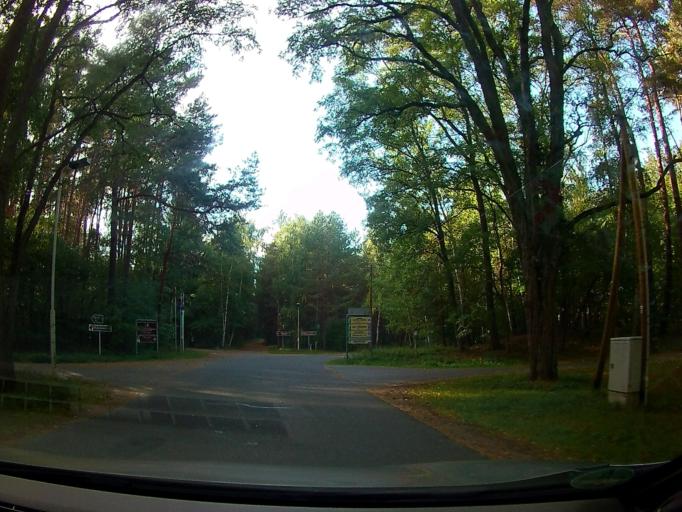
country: DE
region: Mecklenburg-Vorpommern
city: Wesenberg
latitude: 53.2889
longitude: 12.9432
